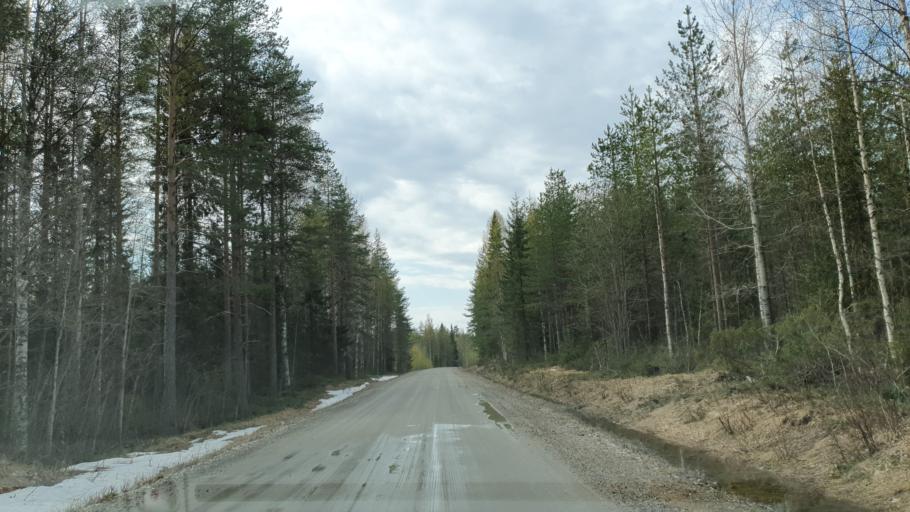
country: FI
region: Kainuu
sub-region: Kehys-Kainuu
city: Kuhmo
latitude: 64.0993
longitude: 29.9377
